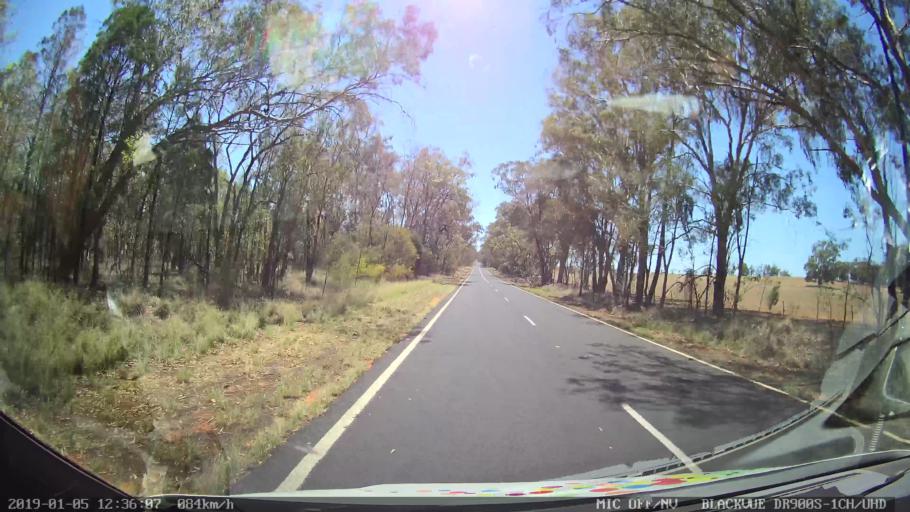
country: AU
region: New South Wales
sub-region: Warrumbungle Shire
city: Coonabarabran
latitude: -31.2079
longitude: 149.4356
